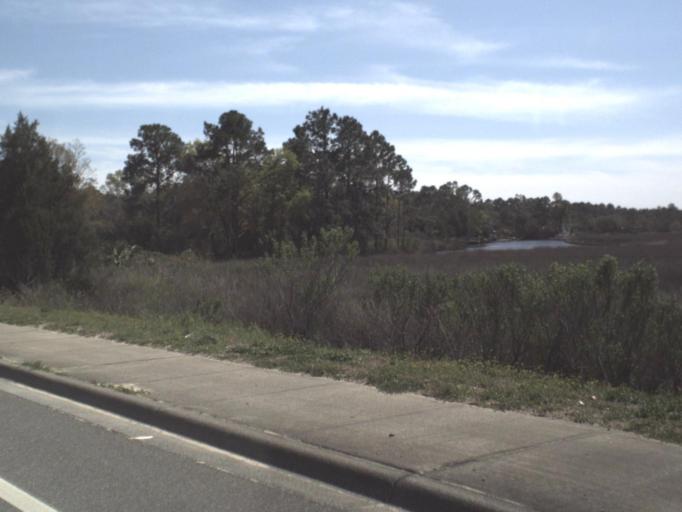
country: US
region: Florida
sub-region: Bay County
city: Lynn Haven
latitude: 30.2875
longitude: -85.6392
